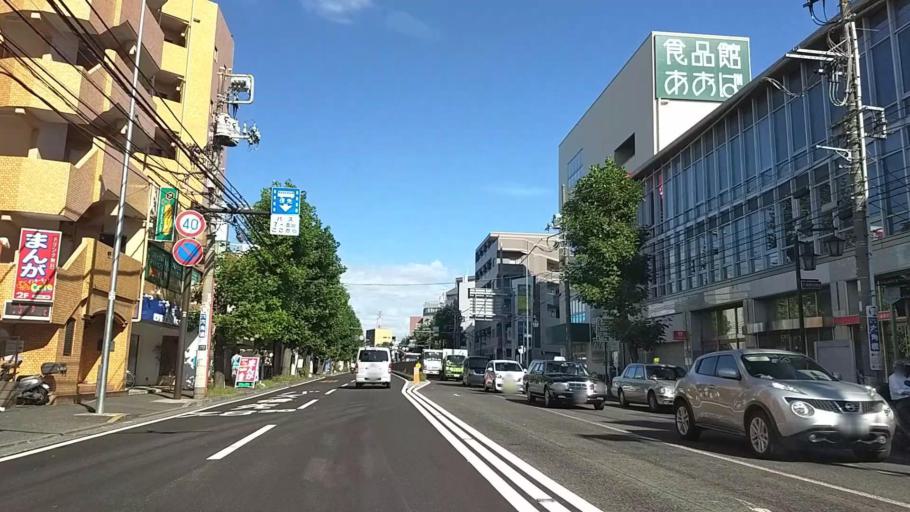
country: JP
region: Kanagawa
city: Yokohama
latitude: 35.4870
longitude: 139.6255
